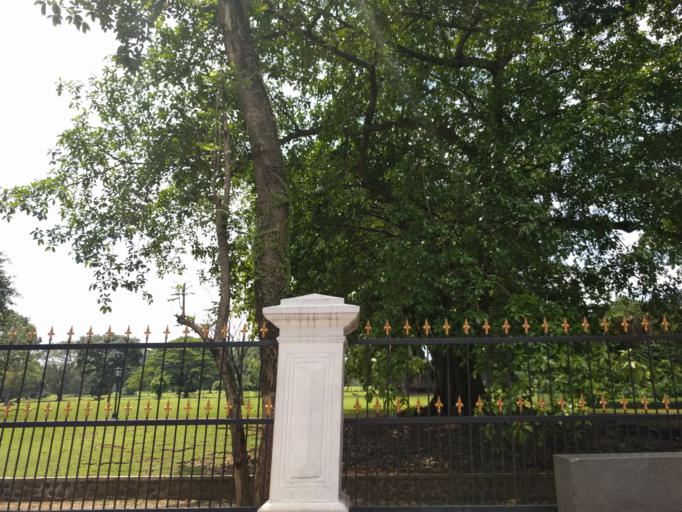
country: ID
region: West Java
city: Bogor
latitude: -6.5953
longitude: 106.7943
